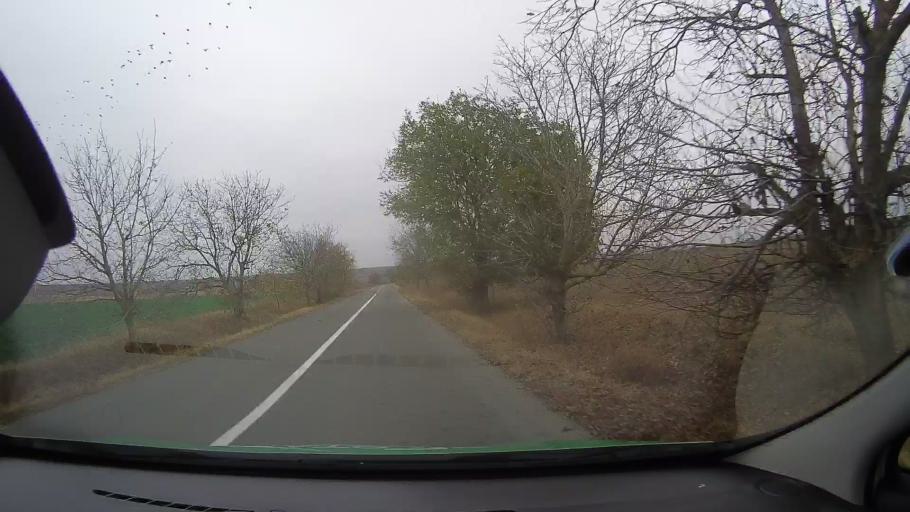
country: RO
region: Constanta
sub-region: Comuna Targusor
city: Targusor
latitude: 44.4830
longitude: 28.3699
